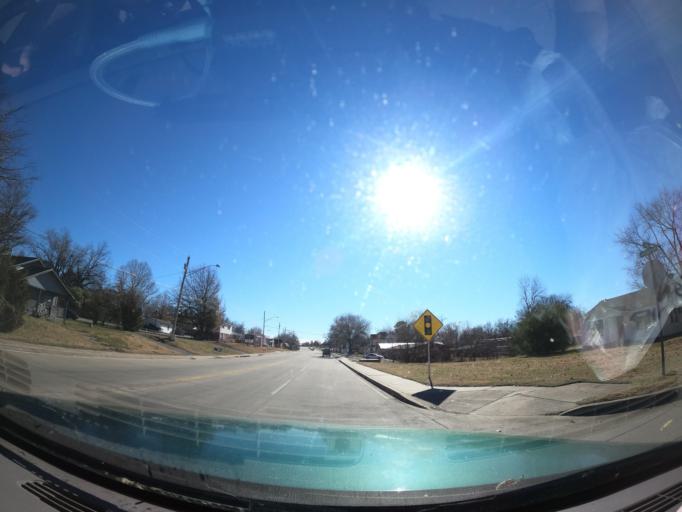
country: US
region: Oklahoma
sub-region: Wagoner County
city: Coweta
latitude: 35.9479
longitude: -95.6506
